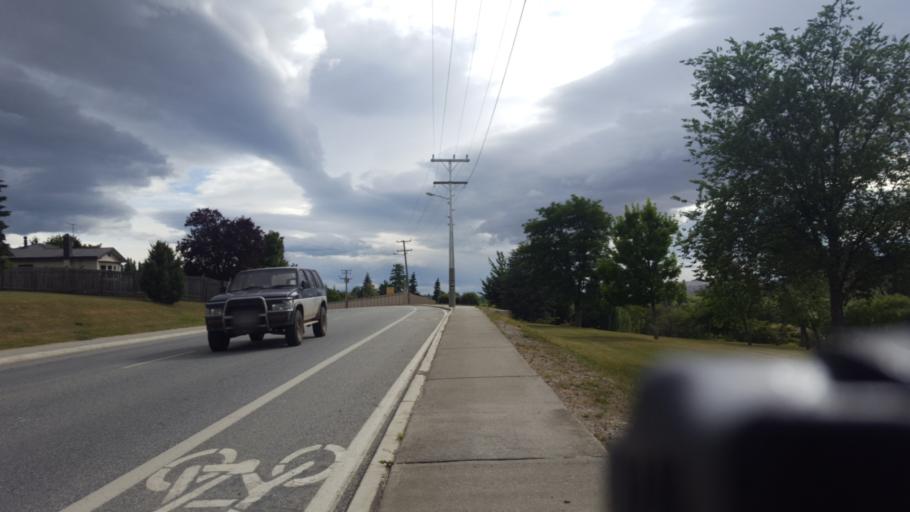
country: NZ
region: Otago
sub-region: Queenstown-Lakes District
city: Wanaka
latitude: -45.2474
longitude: 169.4013
